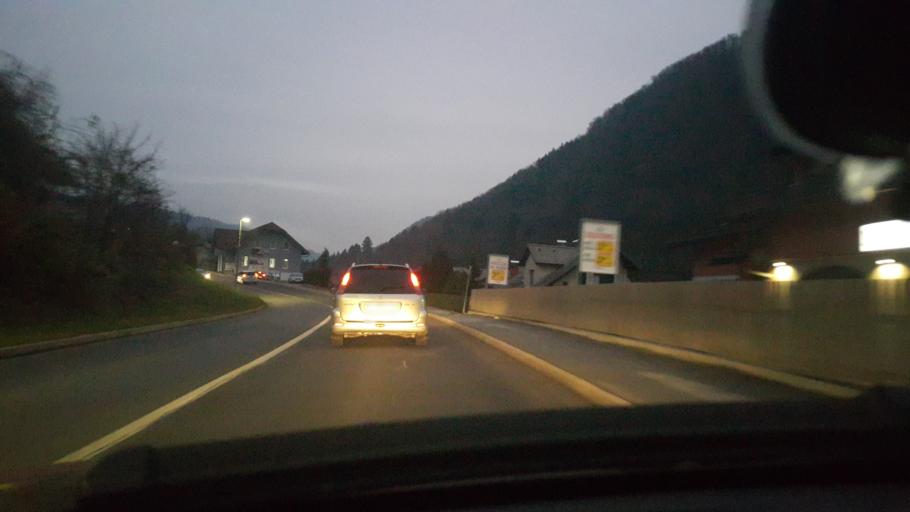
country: SI
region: Dravograd
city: Dravograd
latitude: 46.5896
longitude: 15.0271
